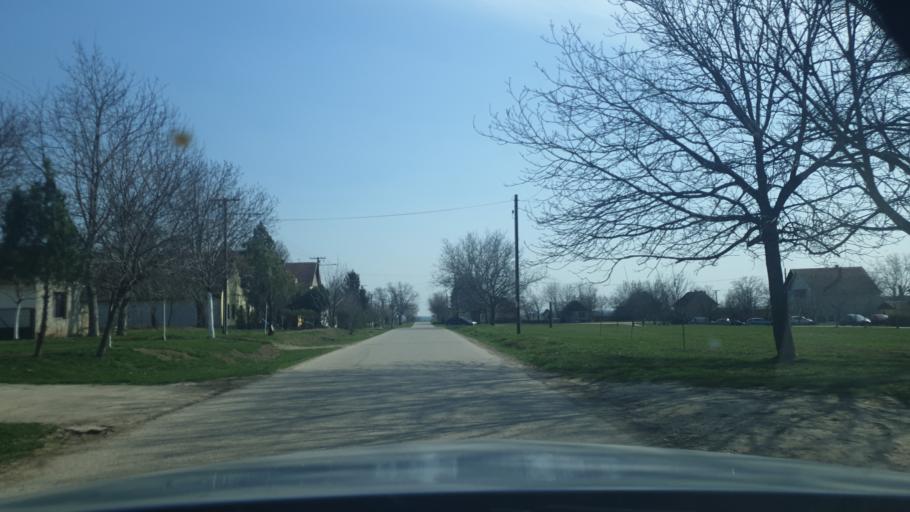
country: RS
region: Autonomna Pokrajina Vojvodina
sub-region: Sremski Okrug
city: Irig
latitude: 45.0617
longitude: 19.9252
